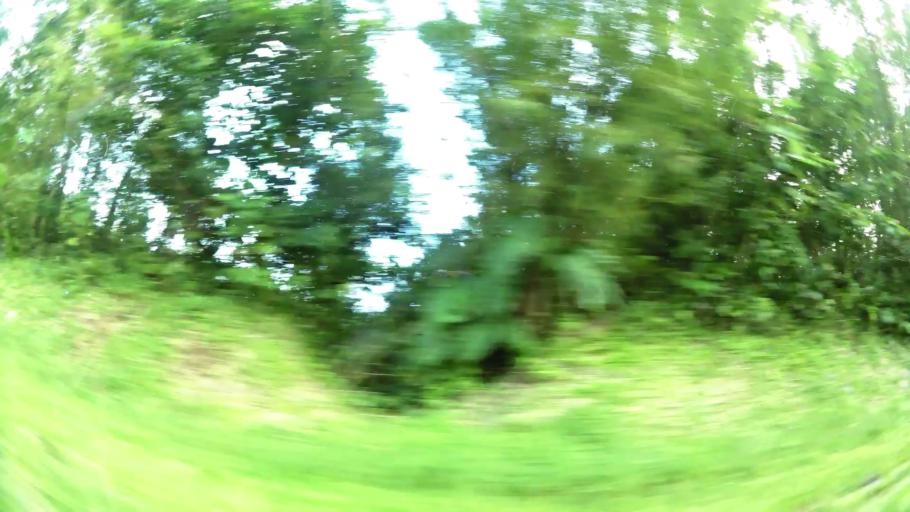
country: GP
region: Guadeloupe
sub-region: Guadeloupe
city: Bouillante
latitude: 16.1791
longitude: -61.7174
